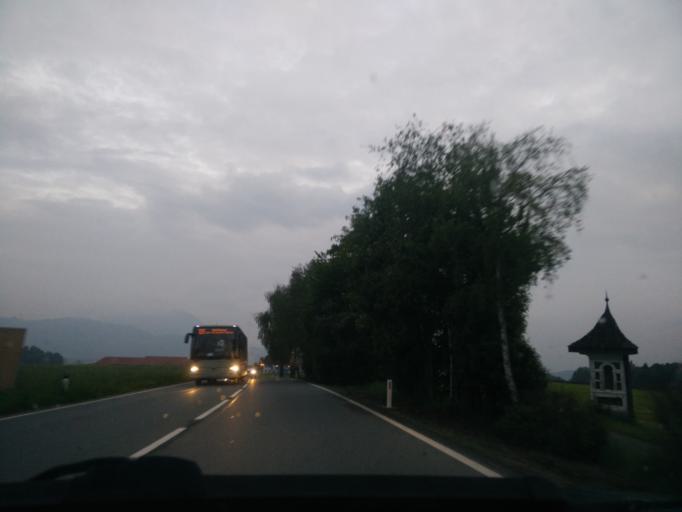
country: AT
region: Salzburg
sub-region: Politischer Bezirk Salzburg-Umgebung
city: Elixhausen
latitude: 47.8784
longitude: 13.0655
